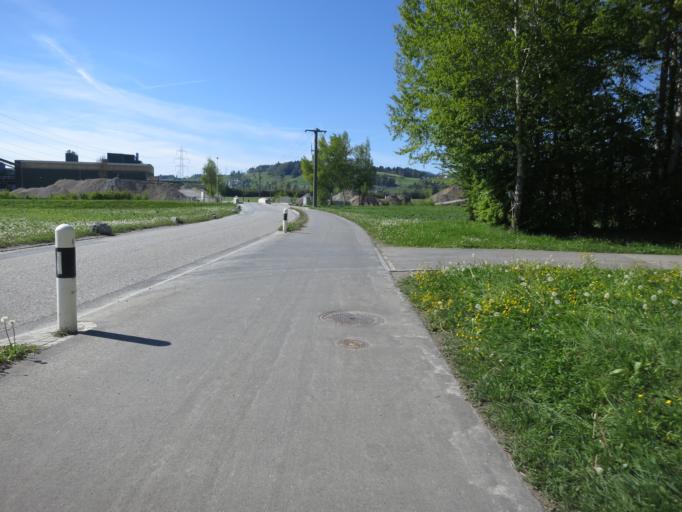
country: CH
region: Saint Gallen
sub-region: Wahlkreis See-Gaster
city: Uznach
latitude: 47.2186
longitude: 8.9709
